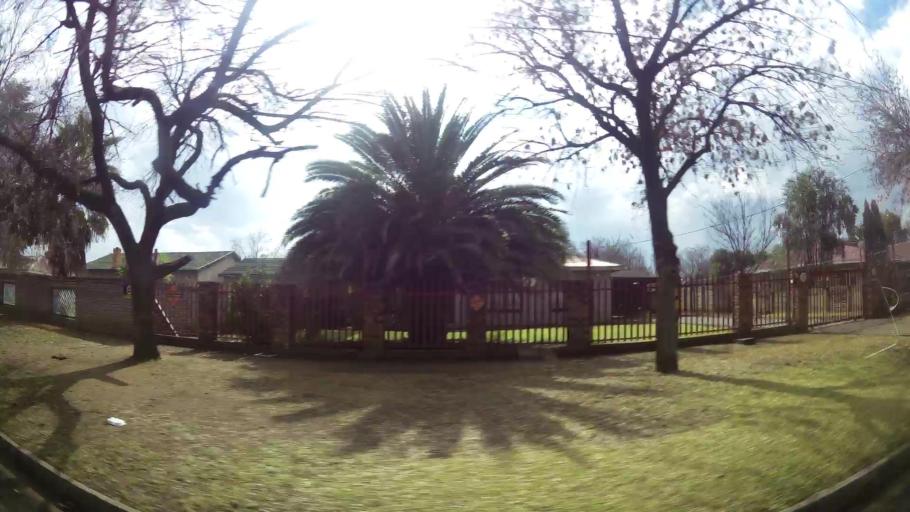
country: ZA
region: Gauteng
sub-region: Sedibeng District Municipality
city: Vereeniging
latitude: -26.6533
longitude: 27.9752
